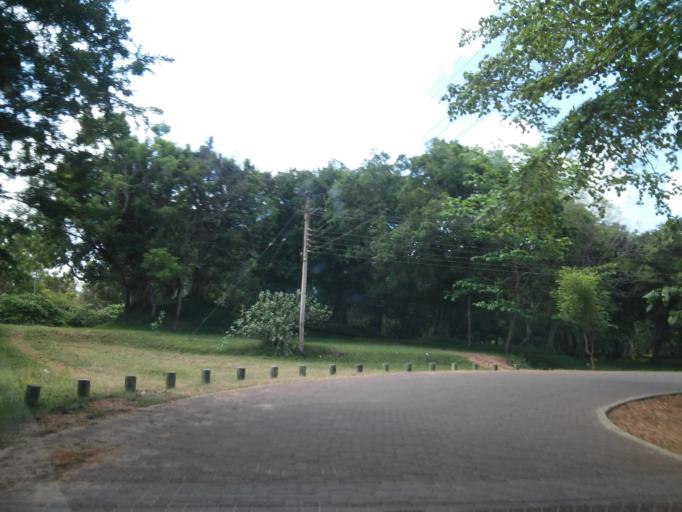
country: LK
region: North Central
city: Anuradhapura
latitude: 8.3702
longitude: 80.3965
